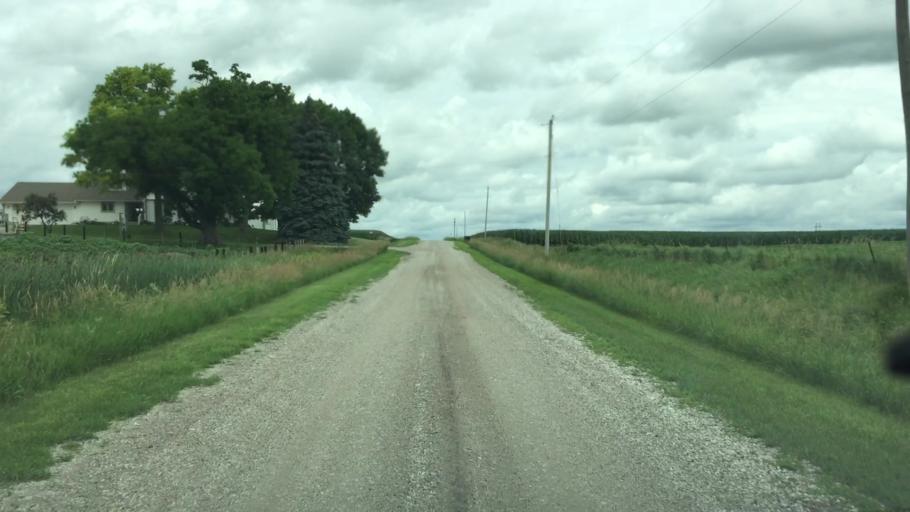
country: US
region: Iowa
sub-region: Jasper County
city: Monroe
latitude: 41.5687
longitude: -93.1208
